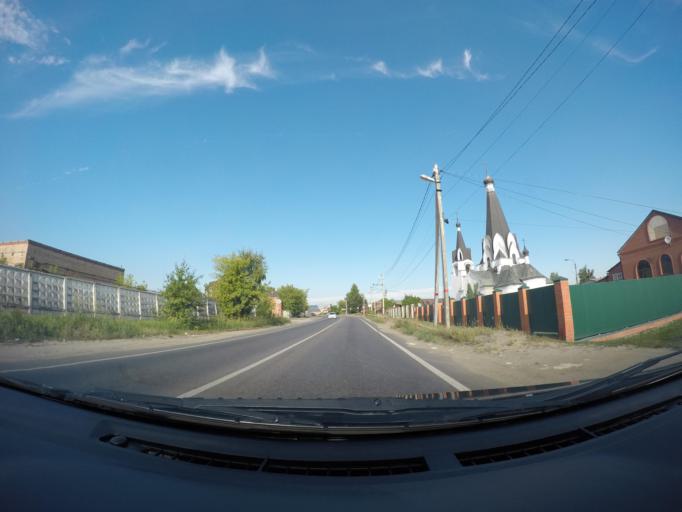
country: RU
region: Moskovskaya
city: Rechitsy
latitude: 55.5904
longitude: 38.5163
